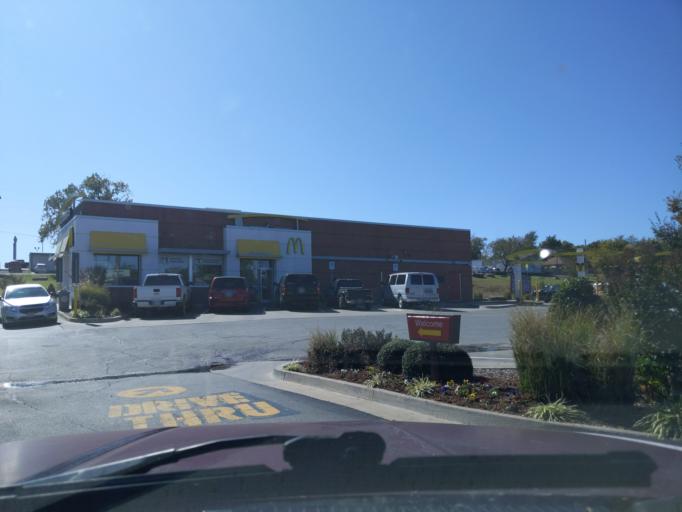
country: US
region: Oklahoma
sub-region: Creek County
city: Bristow
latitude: 35.8397
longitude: -96.3913
